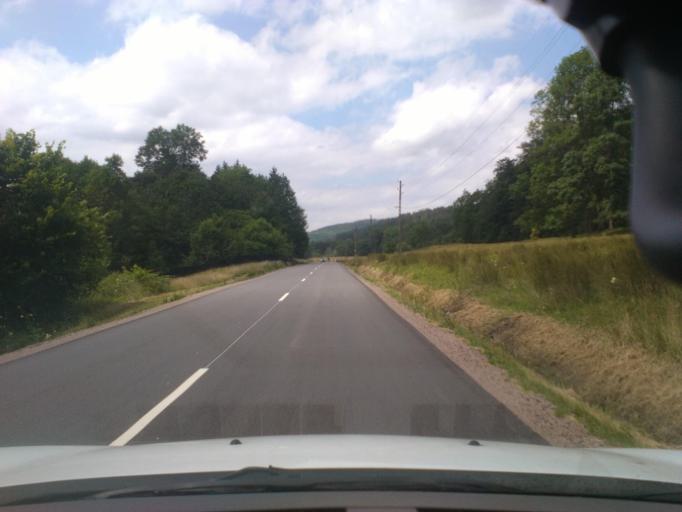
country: FR
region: Lorraine
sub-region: Departement des Vosges
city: Granges-sur-Vologne
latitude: 48.1249
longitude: 6.8351
